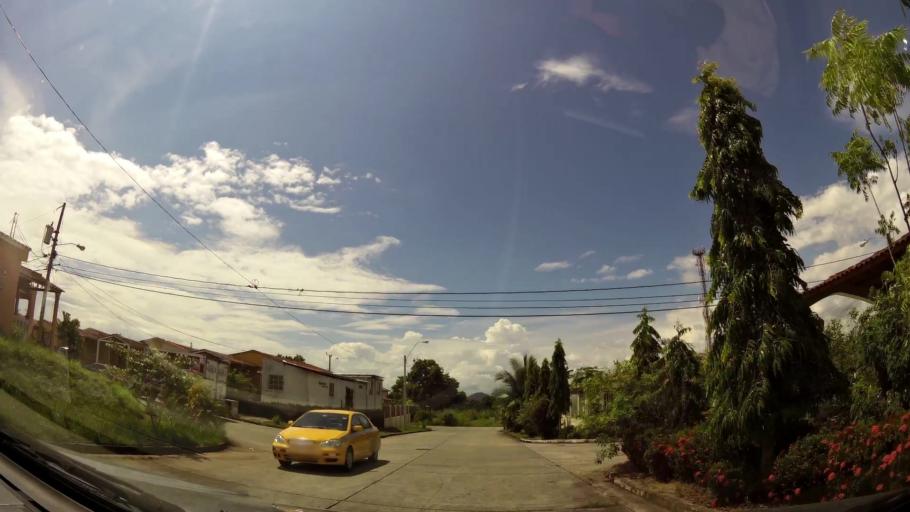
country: PA
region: Panama
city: San Vicente de Bique
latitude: 8.9187
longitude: -79.6918
